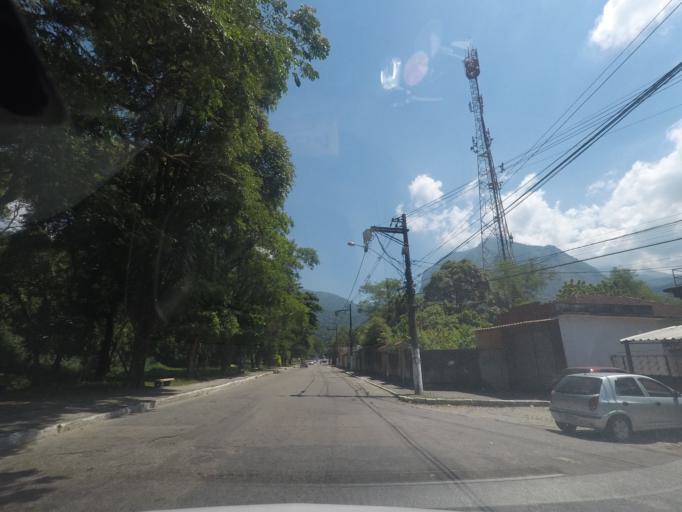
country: BR
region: Rio de Janeiro
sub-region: Petropolis
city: Petropolis
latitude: -22.5756
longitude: -43.1852
